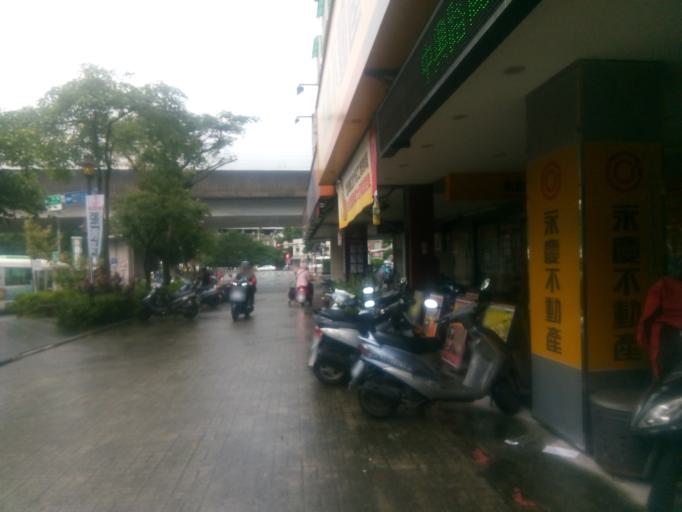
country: TW
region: Taiwan
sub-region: Keelung
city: Keelung
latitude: 25.0687
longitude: 121.6631
